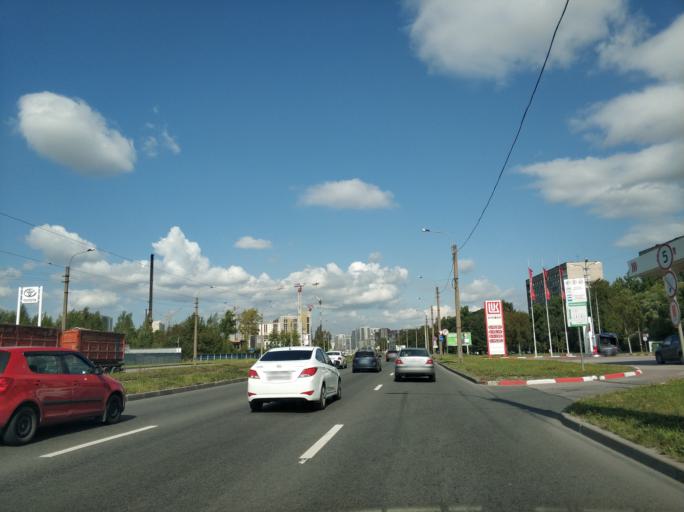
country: RU
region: St.-Petersburg
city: Obukhovo
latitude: 59.8946
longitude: 30.4622
